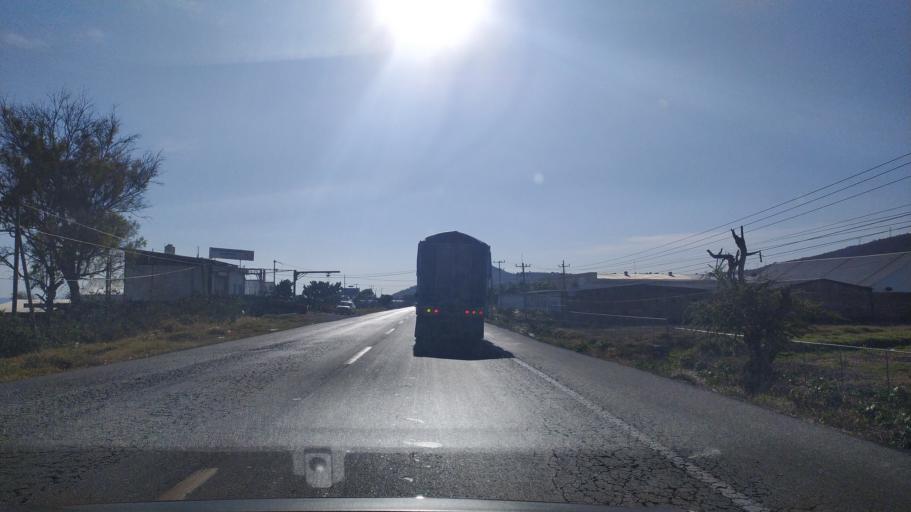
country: MX
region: Jalisco
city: Jamay
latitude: 20.2944
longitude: -102.6869
